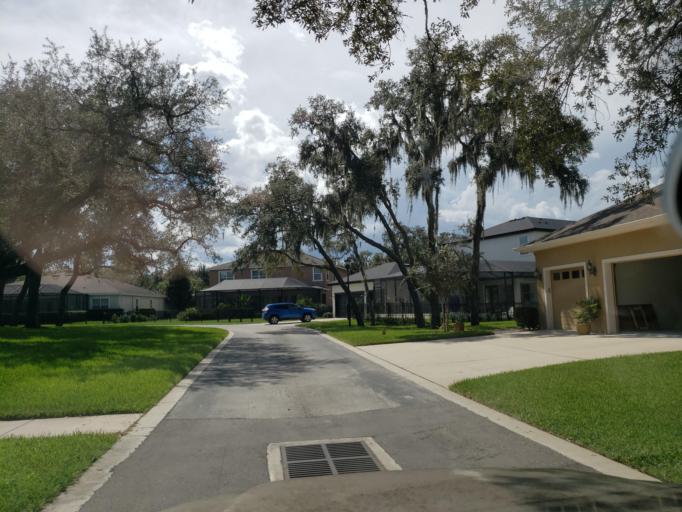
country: US
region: Florida
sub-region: Hillsborough County
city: Fish Hawk
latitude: 27.8469
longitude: -82.2129
